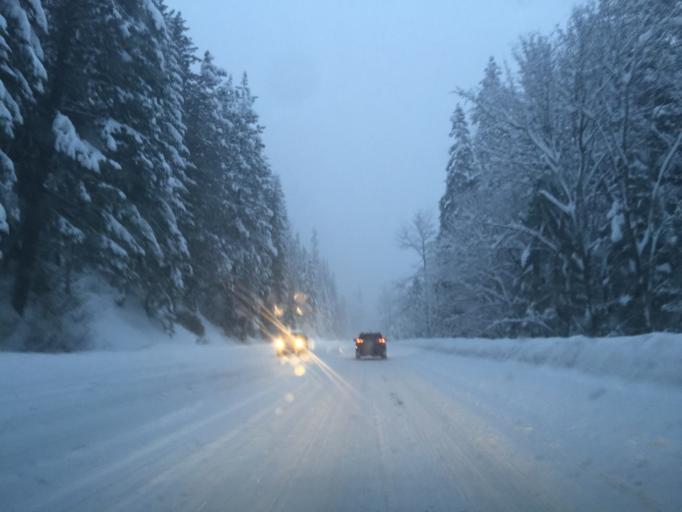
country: US
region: Washington
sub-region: Chelan County
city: Leavenworth
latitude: 47.7910
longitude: -120.8700
